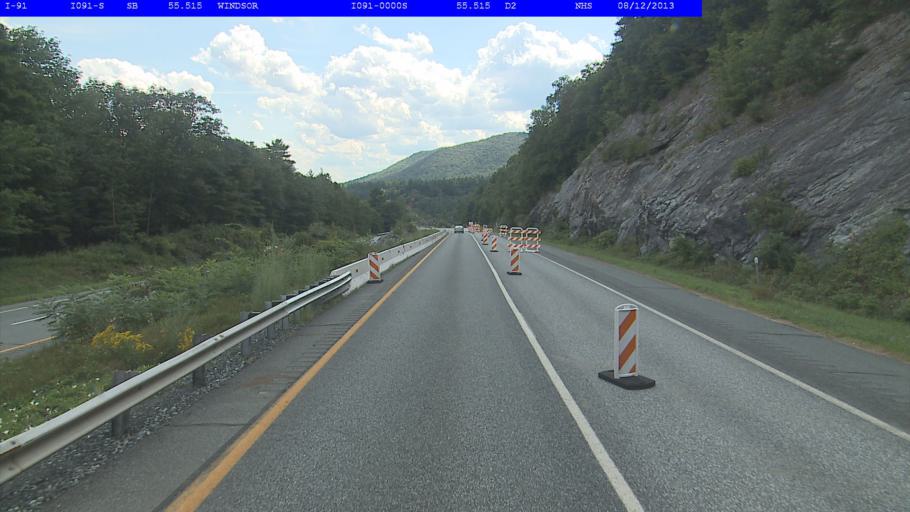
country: US
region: Vermont
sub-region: Windsor County
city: Windsor
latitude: 43.4592
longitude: -72.4059
